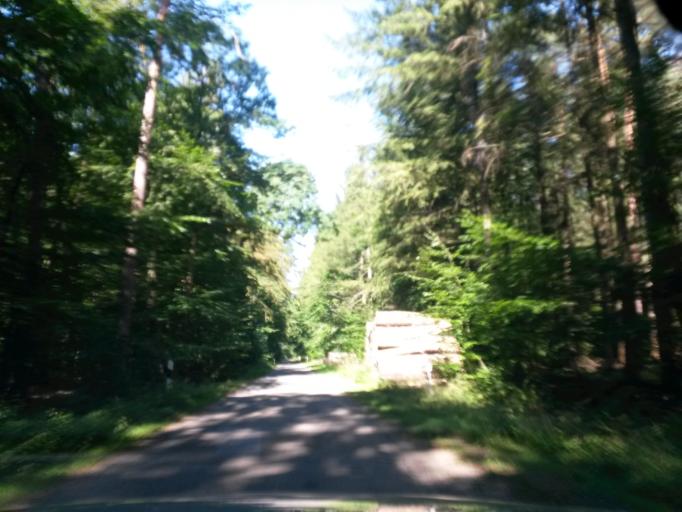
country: DE
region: Brandenburg
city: Templin
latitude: 53.2369
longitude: 13.4549
